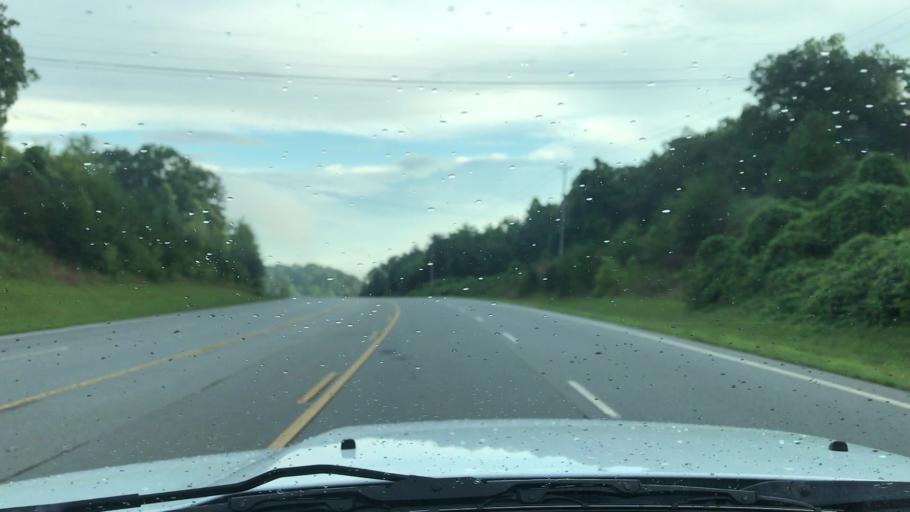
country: US
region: North Carolina
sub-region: Cherokee County
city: Murphy
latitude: 35.0100
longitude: -84.1282
